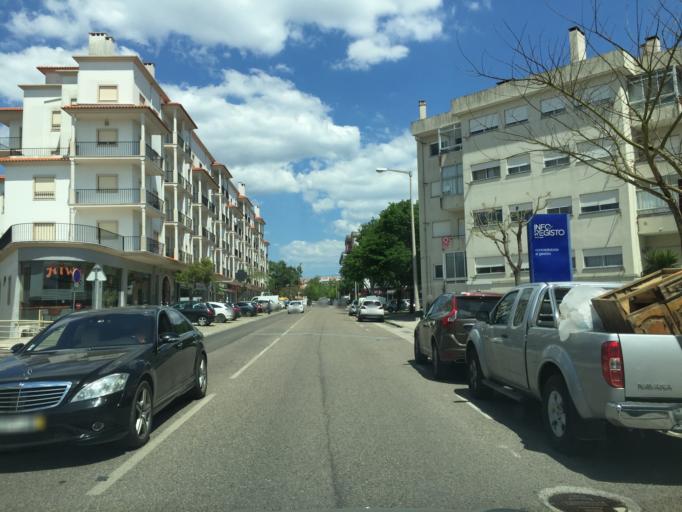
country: PT
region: Santarem
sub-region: Ourem
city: Fatima
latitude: 39.6355
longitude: -8.6803
